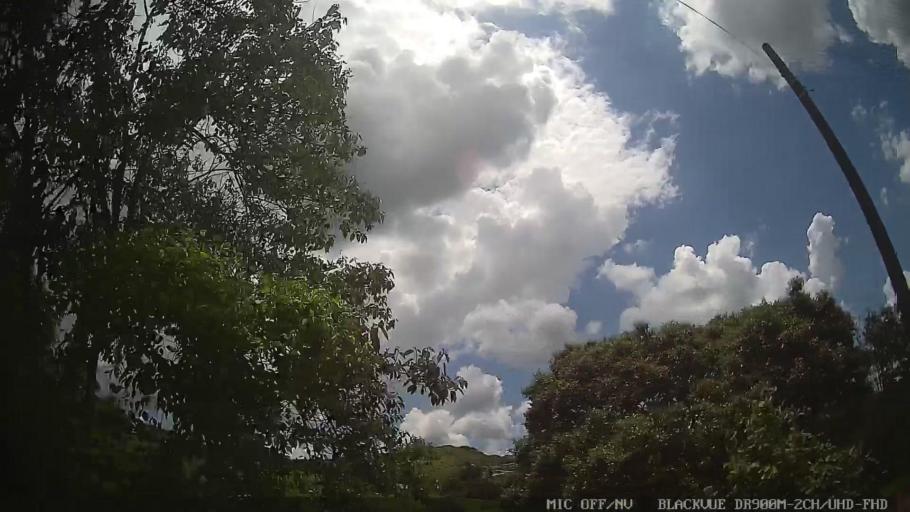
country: BR
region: Sao Paulo
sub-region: Serra Negra
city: Serra Negra
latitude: -22.5933
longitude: -46.7141
